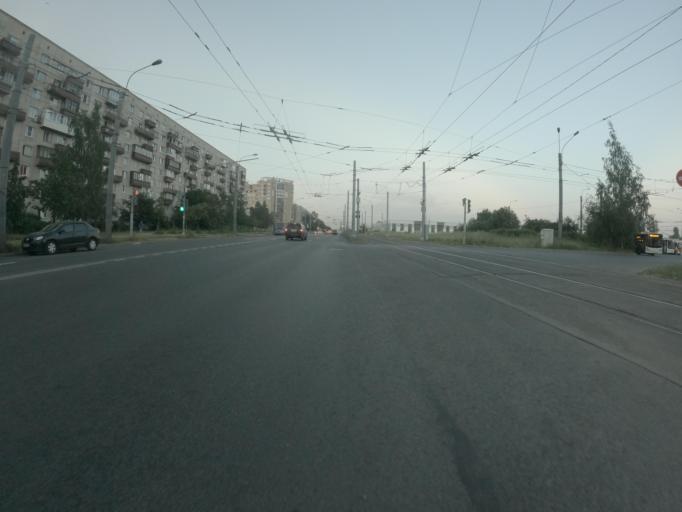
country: RU
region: St.-Petersburg
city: Krasnogvargeisky
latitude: 59.9364
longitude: 30.4848
